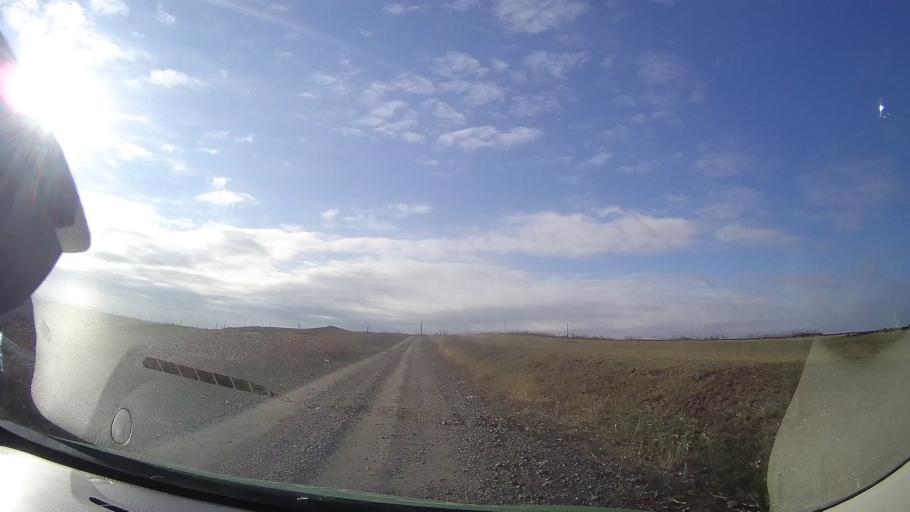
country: RO
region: Mures
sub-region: Comuna Saulia
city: Saulia
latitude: 46.5970
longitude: 24.2217
